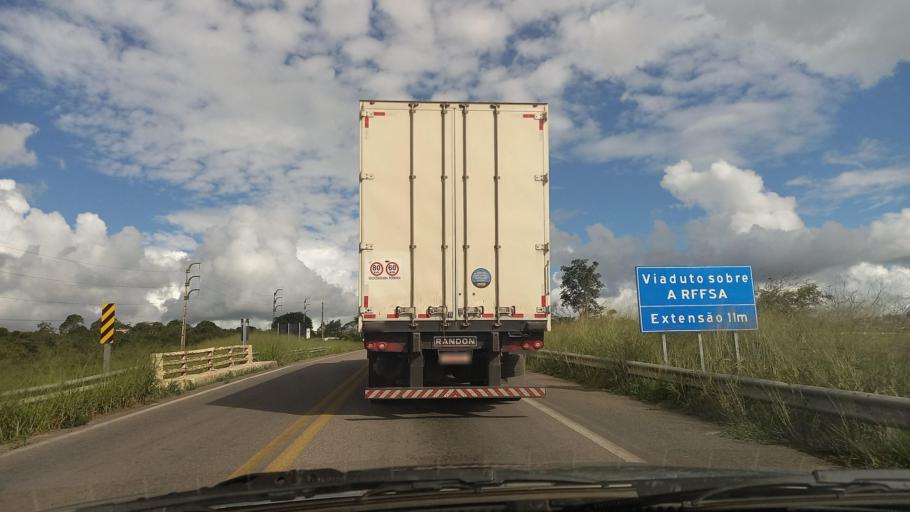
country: BR
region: Pernambuco
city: Garanhuns
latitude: -8.8642
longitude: -36.4630
